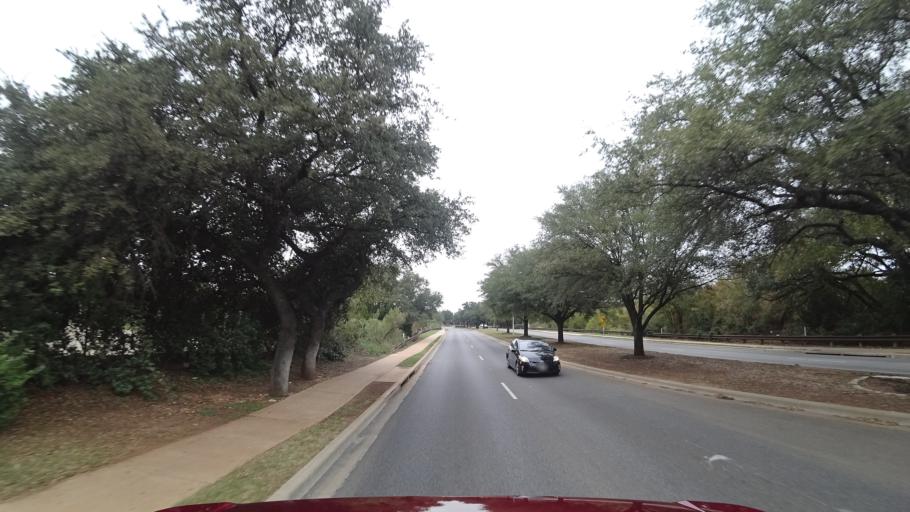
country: US
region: Texas
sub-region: Williamson County
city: Cedar Park
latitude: 30.4889
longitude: -97.8381
